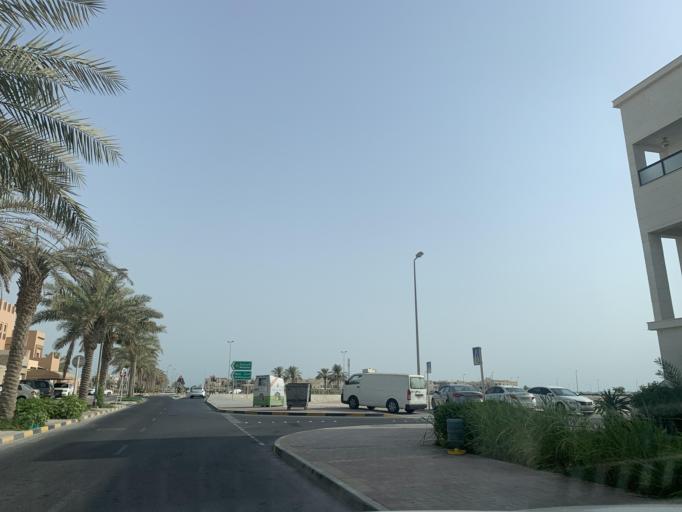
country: BH
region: Manama
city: Jidd Hafs
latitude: 26.2256
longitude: 50.4417
